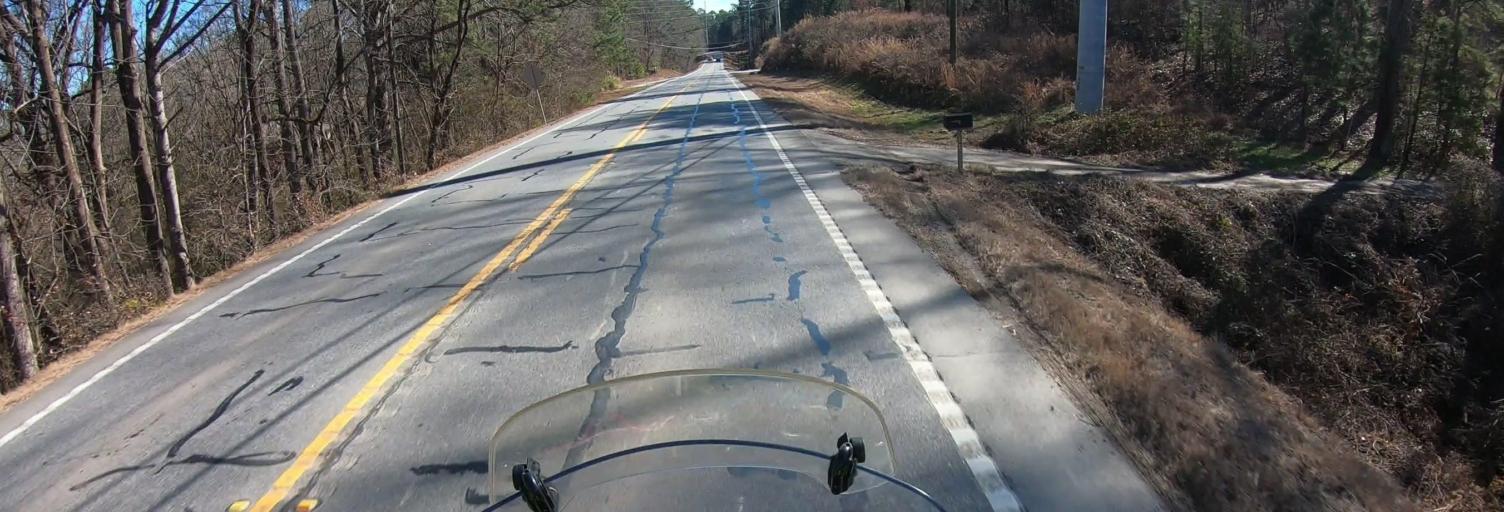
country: US
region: Georgia
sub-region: Forsyth County
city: Cumming
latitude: 34.3044
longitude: -84.2021
